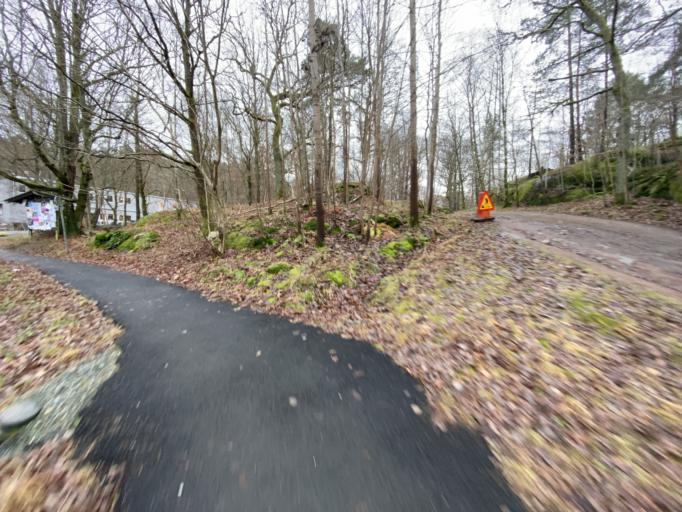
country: SE
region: Vaestra Goetaland
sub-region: Molndal
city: Moelndal
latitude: 57.7106
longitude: 12.0305
